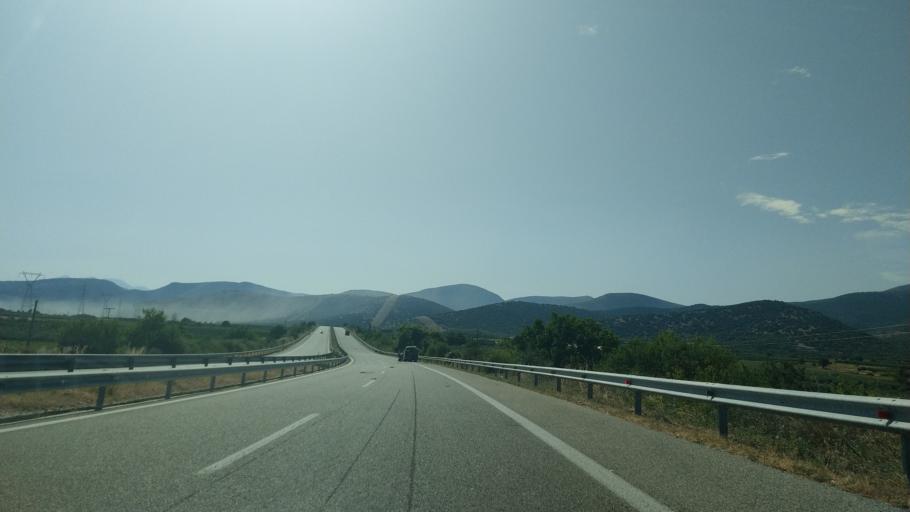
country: GR
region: East Macedonia and Thrace
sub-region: Nomos Kavalas
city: Nea Karvali
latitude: 40.9690
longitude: 24.5144
